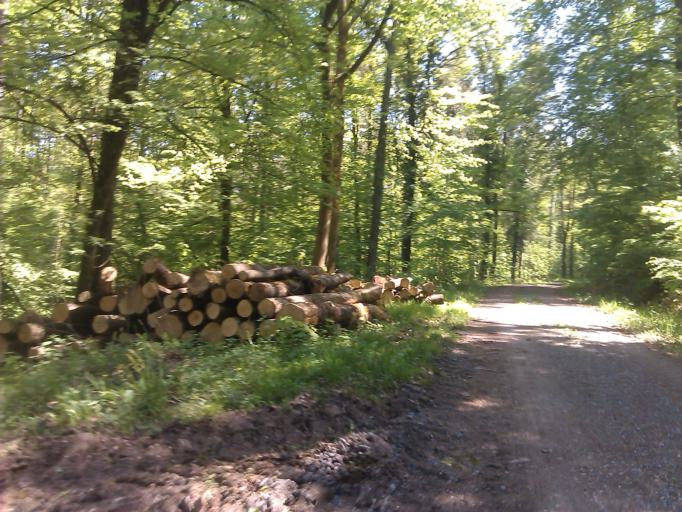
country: DE
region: Baden-Wuerttemberg
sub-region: Regierungsbezirk Stuttgart
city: Zaberfeld
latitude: 49.0443
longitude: 8.9082
